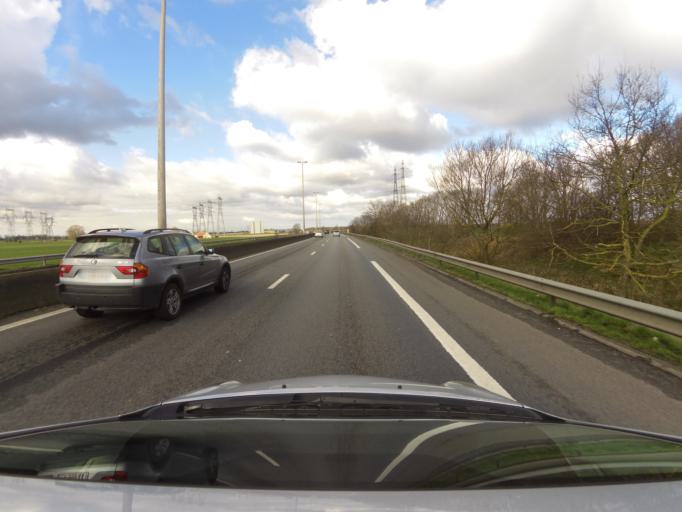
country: FR
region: Nord-Pas-de-Calais
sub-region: Departement du Nord
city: Bourbourg
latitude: 50.9588
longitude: 2.1628
